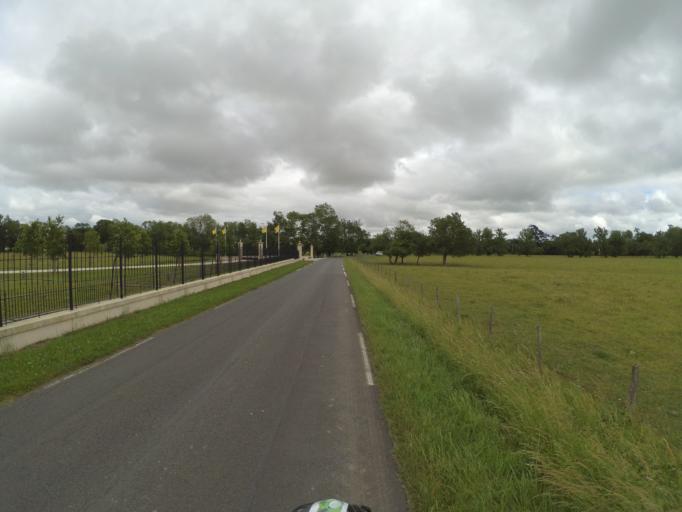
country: FR
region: Aquitaine
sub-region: Departement de la Gironde
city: Macau
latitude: 45.0180
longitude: -0.6223
